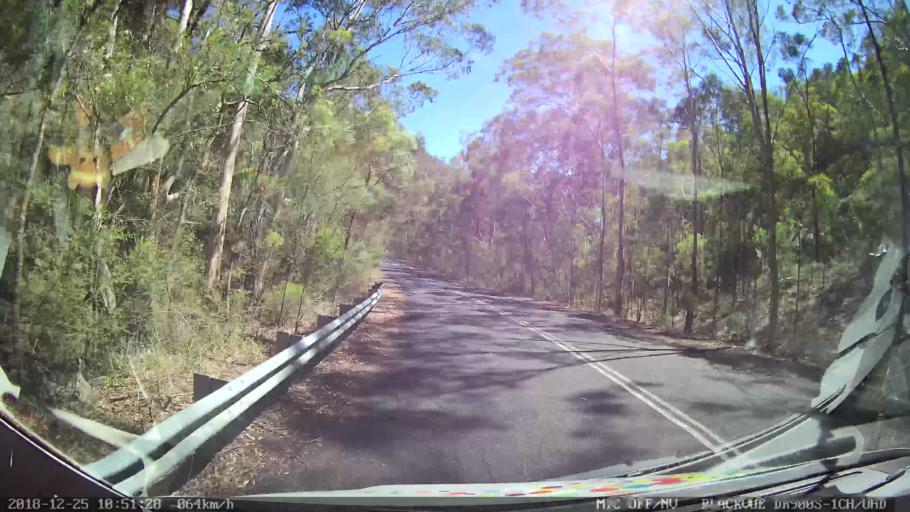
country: AU
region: New South Wales
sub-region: Upper Hunter Shire
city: Merriwa
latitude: -32.4366
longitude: 150.2696
